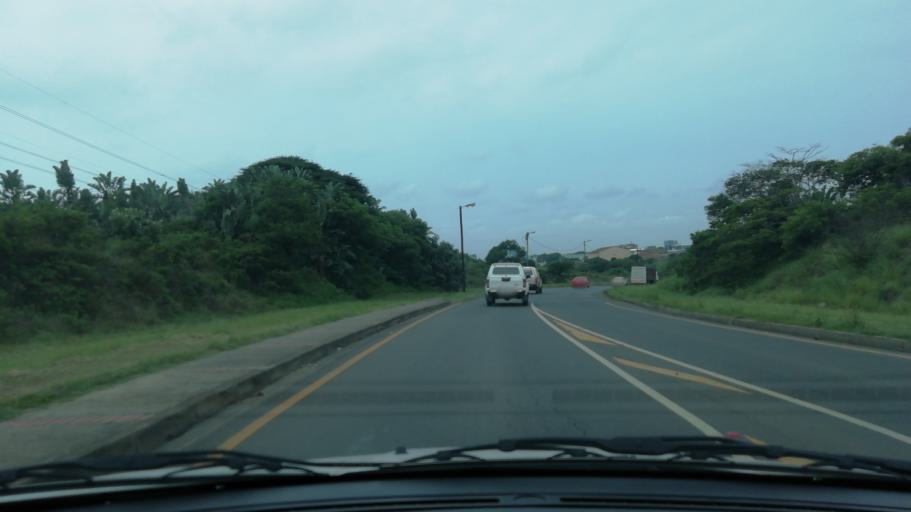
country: ZA
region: KwaZulu-Natal
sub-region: uThungulu District Municipality
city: Richards Bay
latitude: -28.7640
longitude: 32.0380
